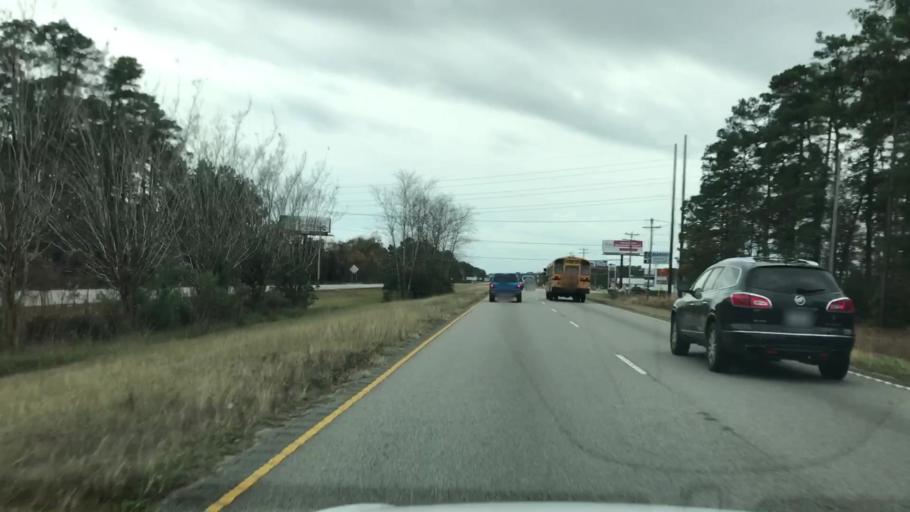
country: US
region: South Carolina
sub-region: Horry County
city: Garden City
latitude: 33.6093
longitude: -79.0132
